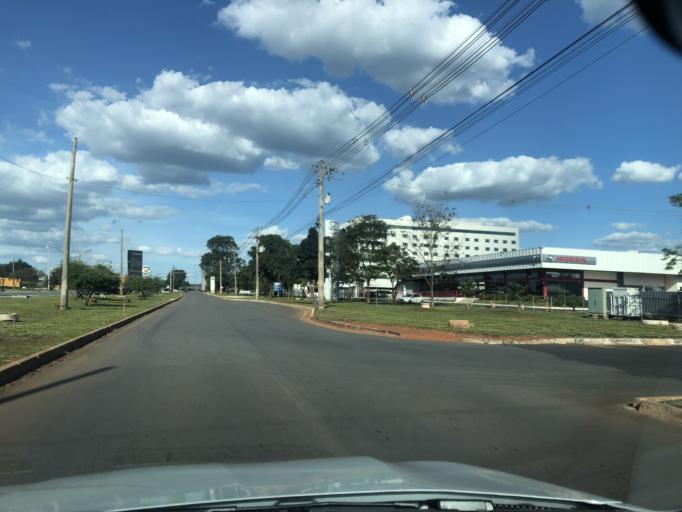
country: BR
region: Federal District
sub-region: Brasilia
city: Brasilia
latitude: -15.8706
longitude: -47.9287
